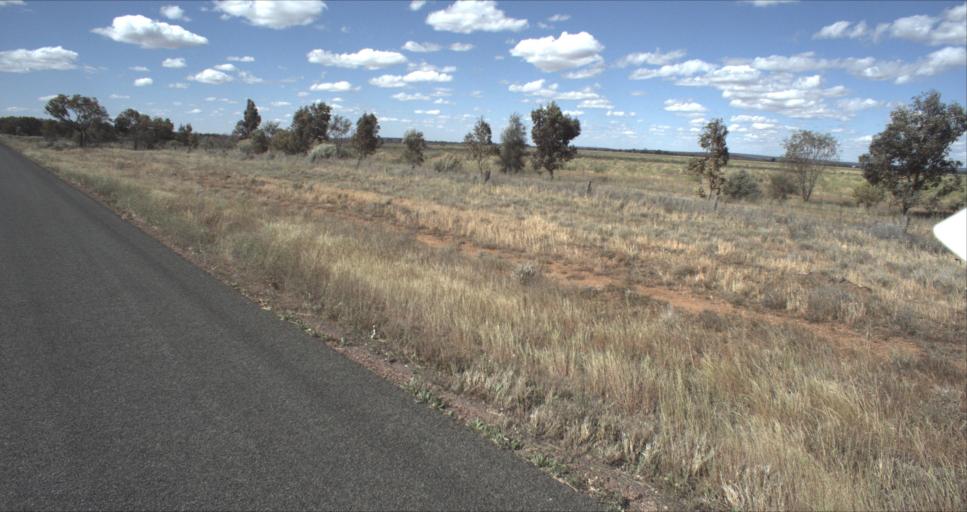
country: AU
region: New South Wales
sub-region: Leeton
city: Leeton
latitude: -34.4348
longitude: 146.2575
